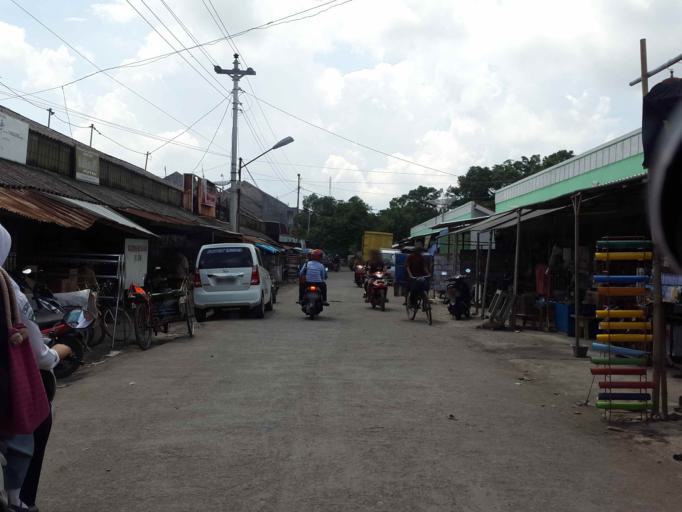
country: ID
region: Central Java
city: Petarukan
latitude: -6.8925
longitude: 109.4568
